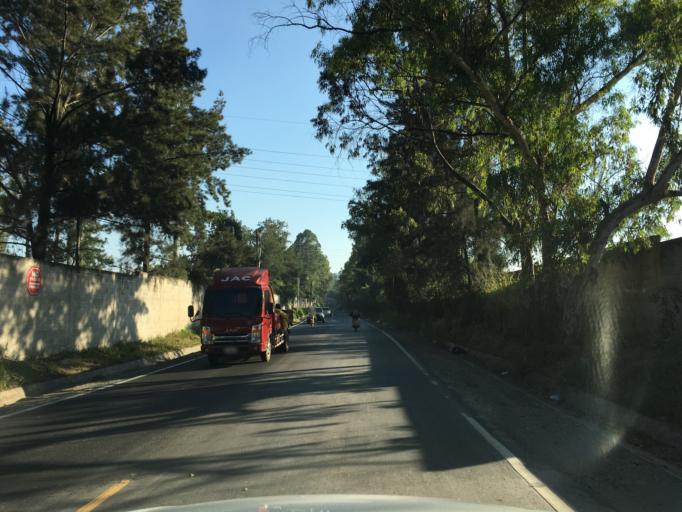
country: GT
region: Guatemala
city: Villa Nueva
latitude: 14.5248
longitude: -90.6168
